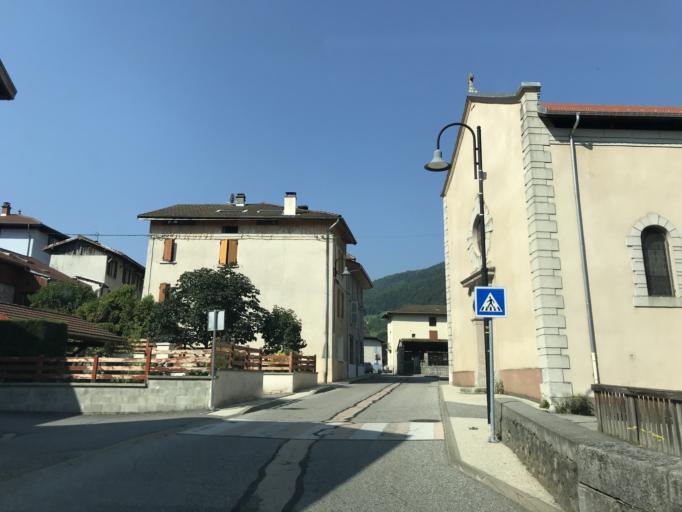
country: FR
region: Rhone-Alpes
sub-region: Departement de l'Isere
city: Allevard
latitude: 45.4234
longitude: 6.0965
